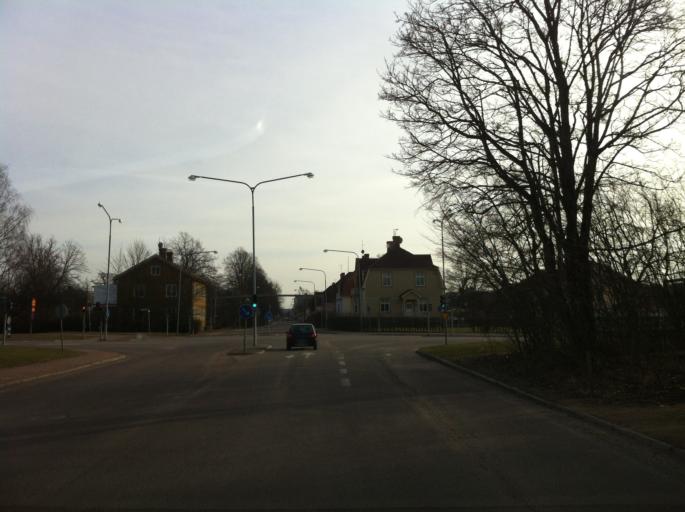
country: SE
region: Vaermland
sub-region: Kristinehamns Kommun
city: Kristinehamn
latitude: 59.3161
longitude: 14.1055
